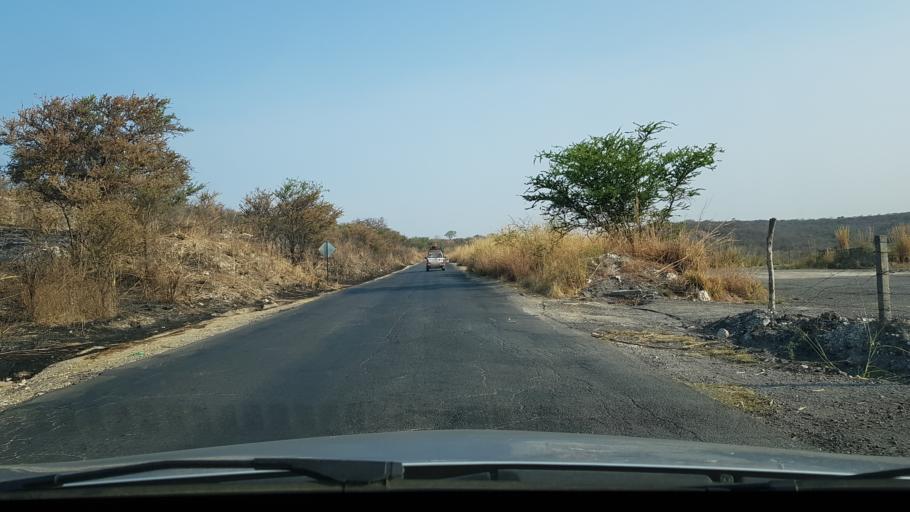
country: MX
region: Morelos
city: Tlaltizapan
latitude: 18.6588
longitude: -99.0455
